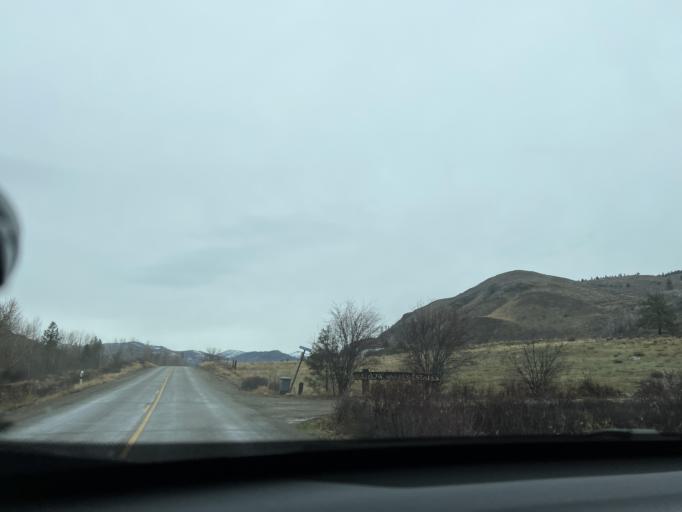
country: US
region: Washington
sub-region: Okanogan County
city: Brewster
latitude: 48.5228
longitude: -120.1784
